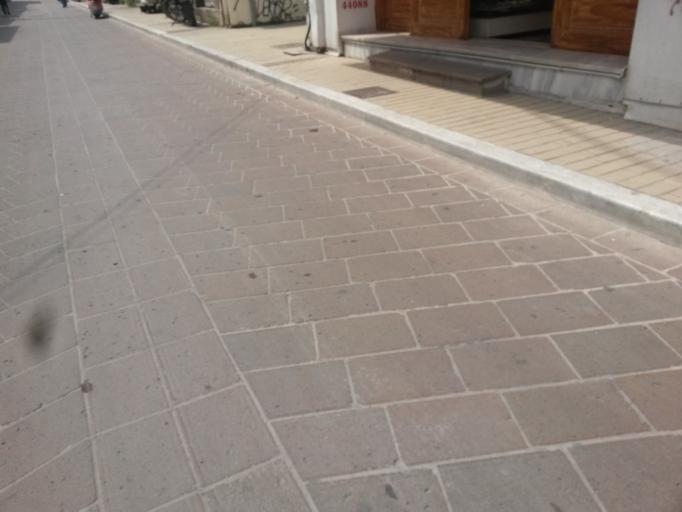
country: GR
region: North Aegean
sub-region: Nomos Lesvou
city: Mytilini
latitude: 39.1114
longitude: 26.5575
